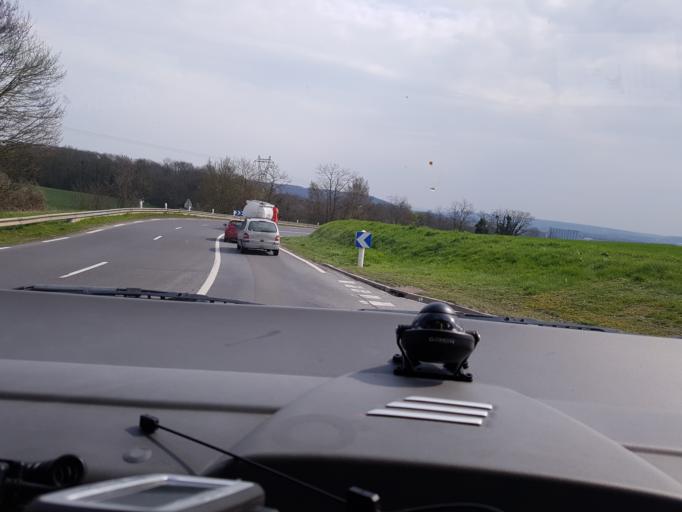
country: FR
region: Picardie
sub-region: Departement de l'Aisne
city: Cuffies
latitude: 49.4059
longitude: 3.3360
